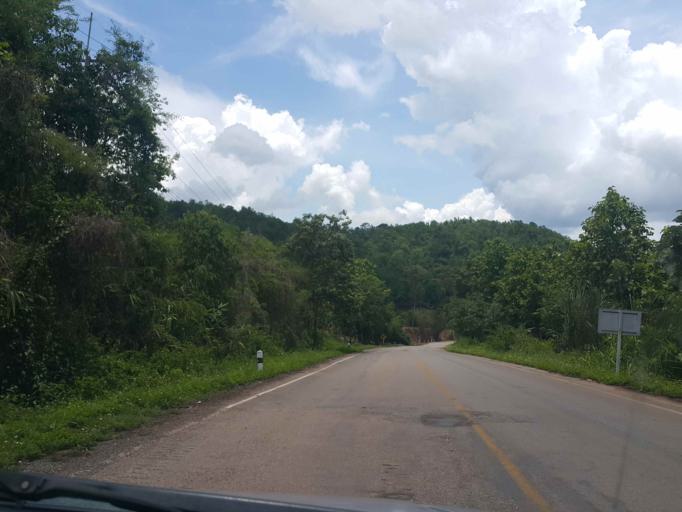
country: TH
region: Phayao
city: Chiang Muan
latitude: 18.8980
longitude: 100.1416
